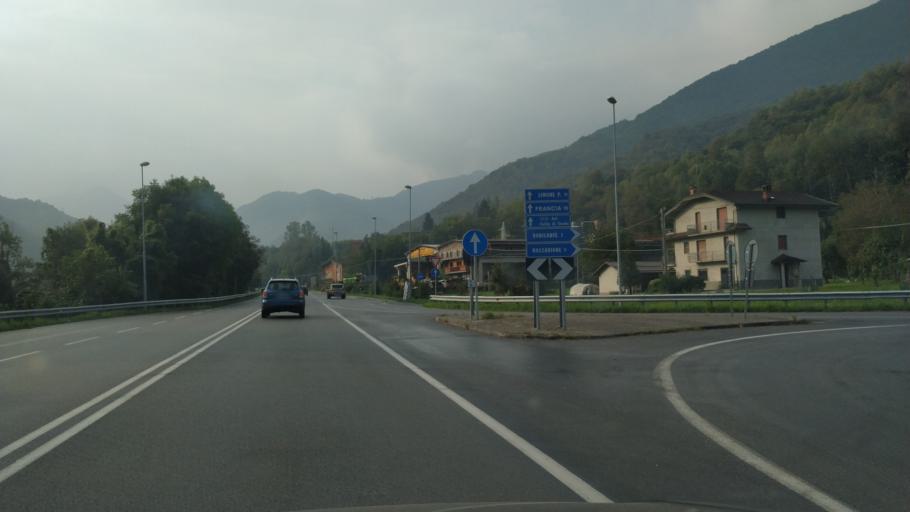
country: IT
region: Piedmont
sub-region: Provincia di Cuneo
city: Robilante
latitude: 44.2798
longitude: 7.5175
